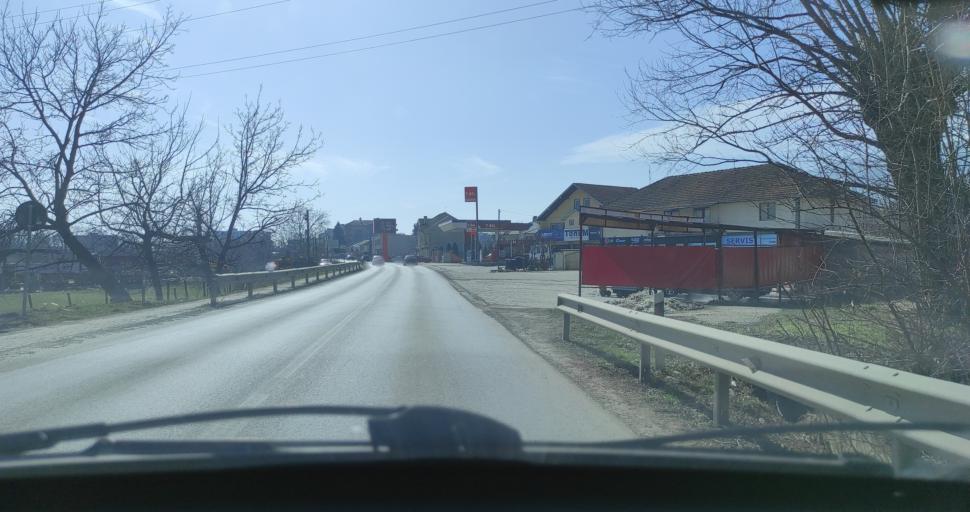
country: XK
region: Gjakova
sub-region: Komuna e Decanit
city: Decan
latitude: 42.5509
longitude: 20.2908
